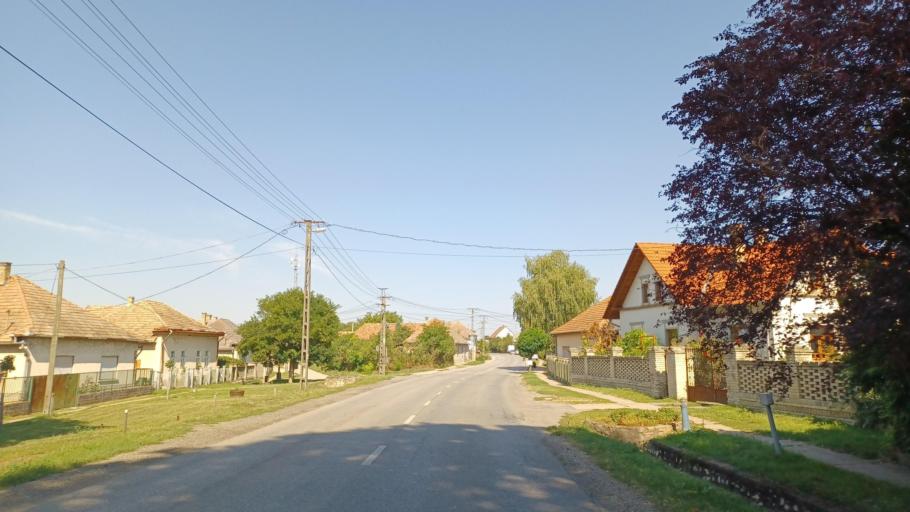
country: HU
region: Tolna
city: Nagydorog
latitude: 46.6297
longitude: 18.6554
